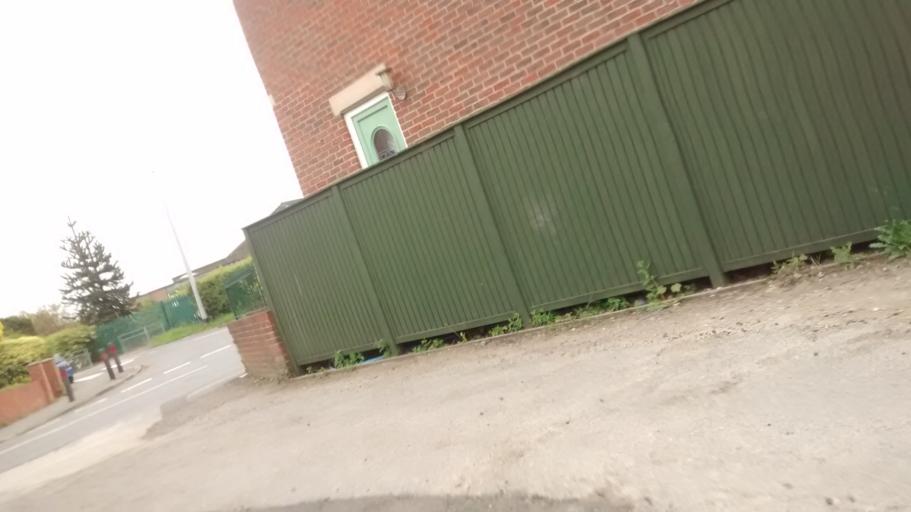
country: GB
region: England
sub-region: County Durham
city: Pittington
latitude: 54.7916
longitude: -1.4881
